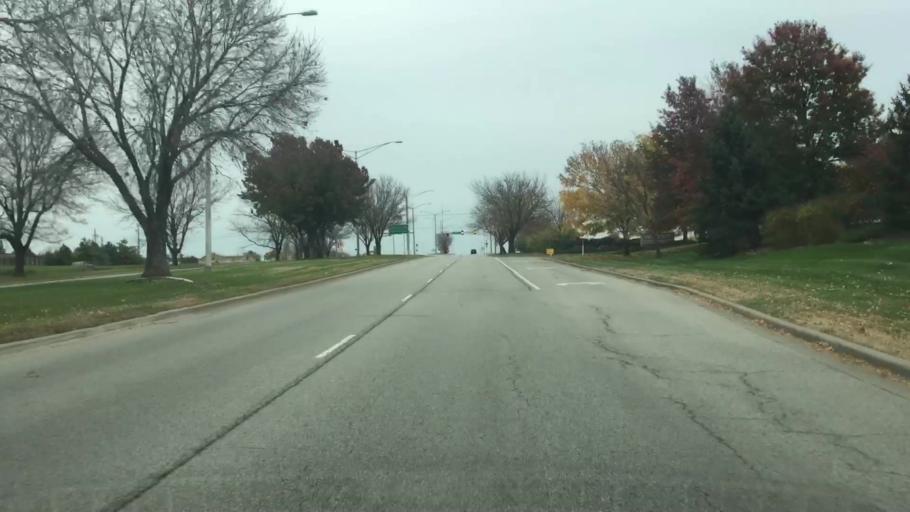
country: US
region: Kansas
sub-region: Johnson County
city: Lenexa
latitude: 38.9272
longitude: -94.7636
